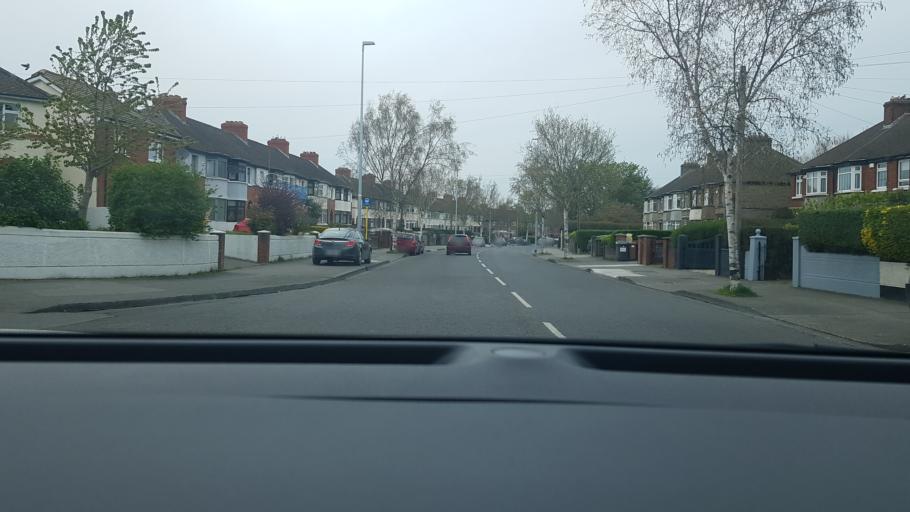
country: IE
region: Leinster
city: Rialto
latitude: 53.3272
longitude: -6.2978
